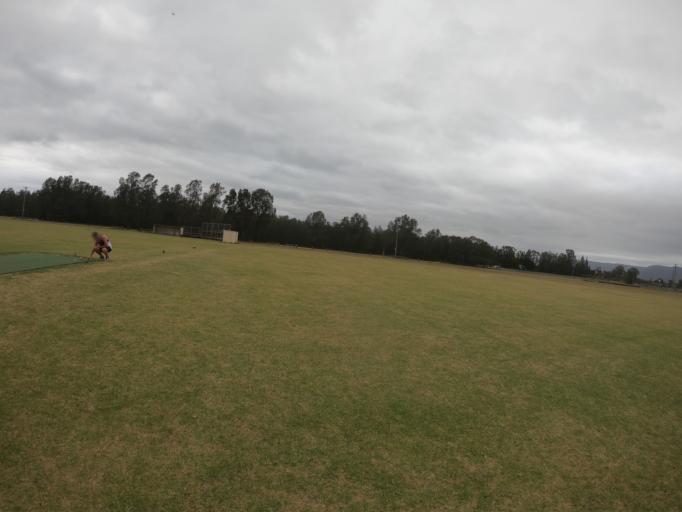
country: AU
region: New South Wales
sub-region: Wollongong
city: Berkeley
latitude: -34.4832
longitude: 150.8345
